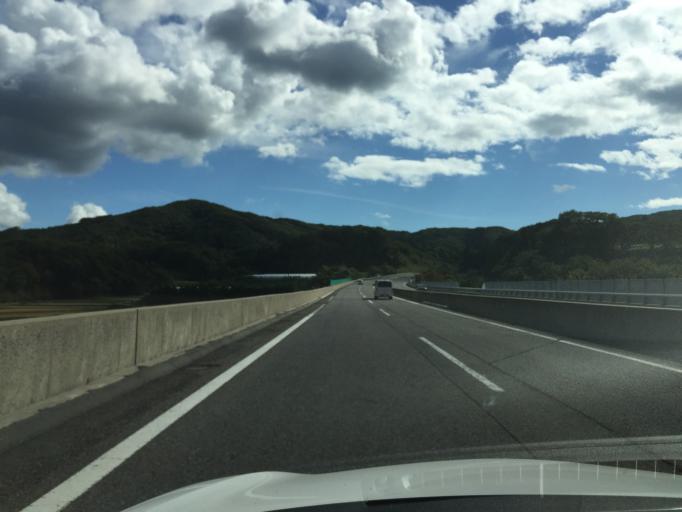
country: JP
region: Fukushima
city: Funehikimachi-funehiki
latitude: 37.3611
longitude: 140.6082
